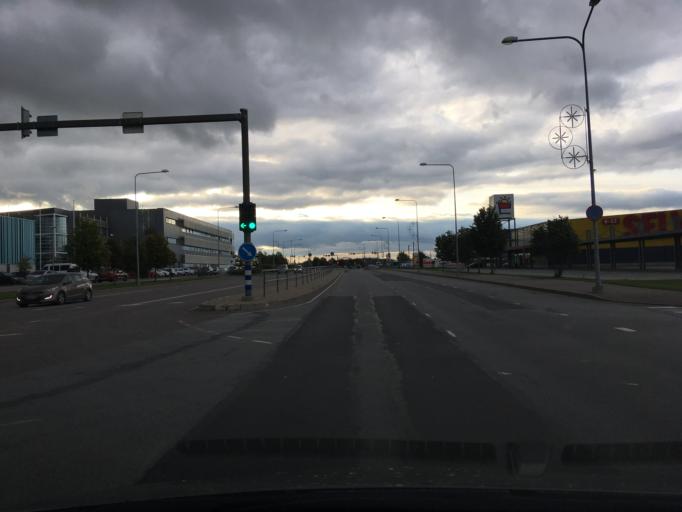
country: EE
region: Harju
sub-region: Tallinna linn
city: Kose
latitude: 59.4388
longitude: 24.8700
